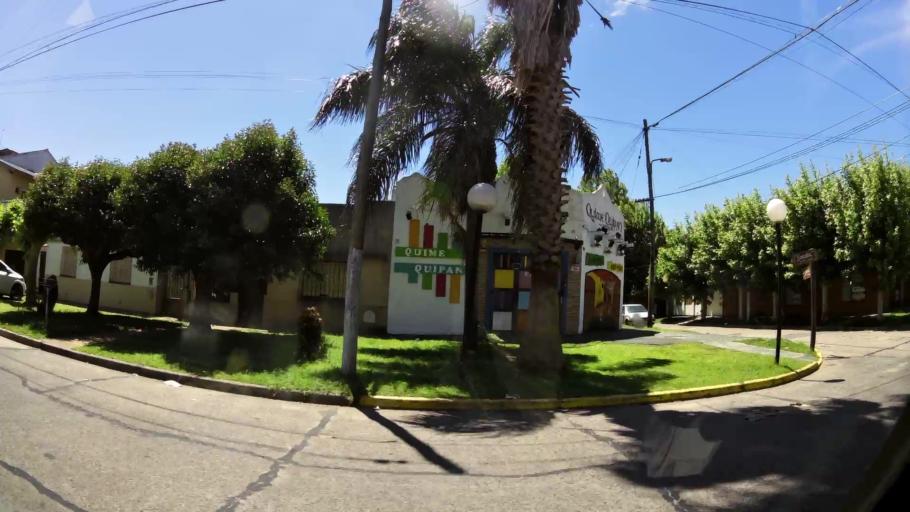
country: AR
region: Buenos Aires
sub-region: Partido de Quilmes
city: Quilmes
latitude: -34.7179
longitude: -58.2802
